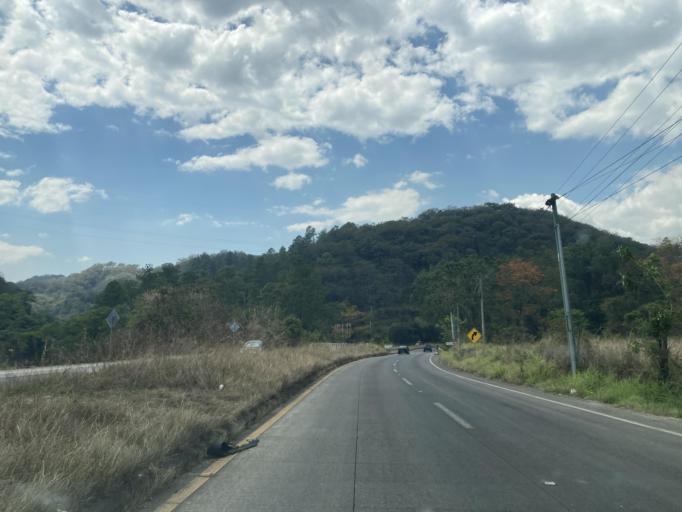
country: GT
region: Santa Rosa
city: Barberena
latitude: 14.3379
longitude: -90.4409
